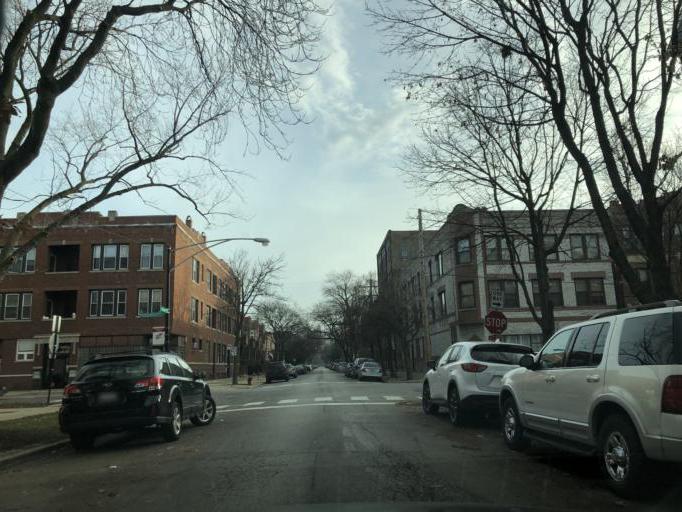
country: US
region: Illinois
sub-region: Cook County
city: Chicago
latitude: 41.8977
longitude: -87.6824
